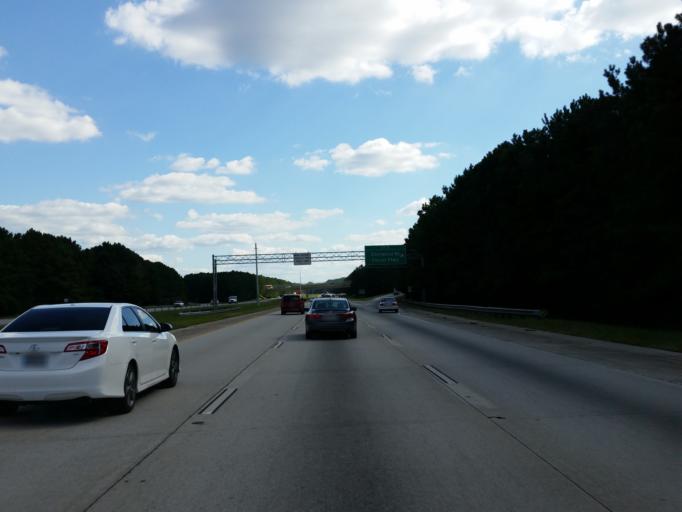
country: US
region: Georgia
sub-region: Clayton County
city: Lake City
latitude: 33.6170
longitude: -84.2974
